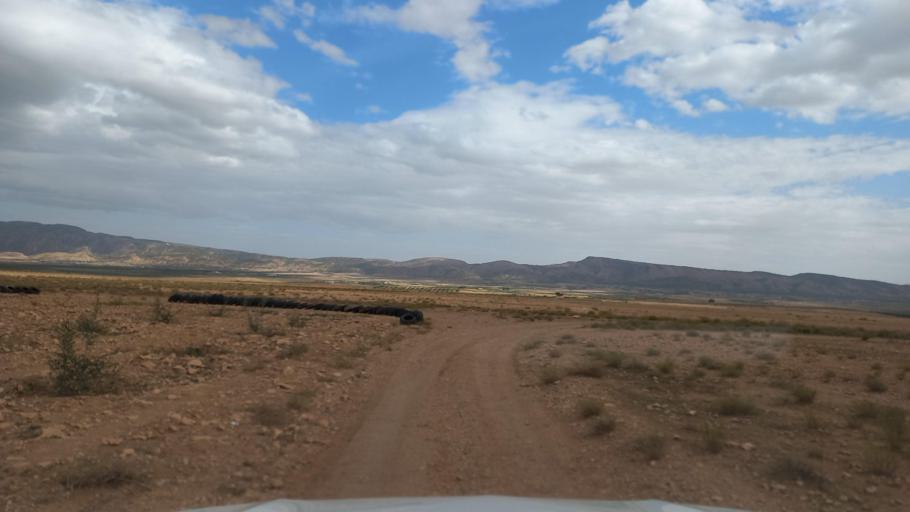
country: TN
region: Al Qasrayn
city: Sbiba
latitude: 35.3871
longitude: 9.1046
